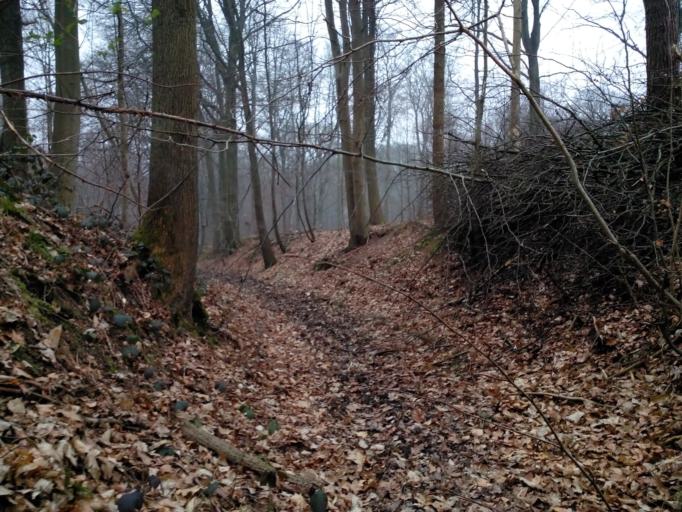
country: BE
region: Flanders
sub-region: Provincie Vlaams-Brabant
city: Bierbeek
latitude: 50.8141
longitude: 4.7207
